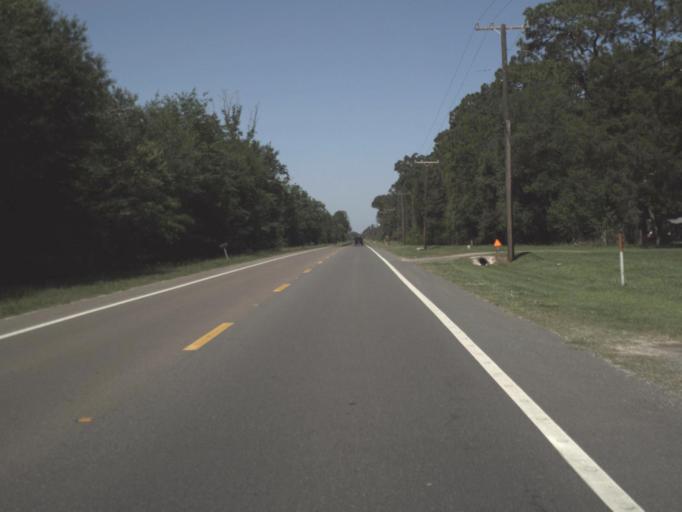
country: US
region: Florida
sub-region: Baker County
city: Macclenny
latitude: 30.2721
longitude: -82.1804
